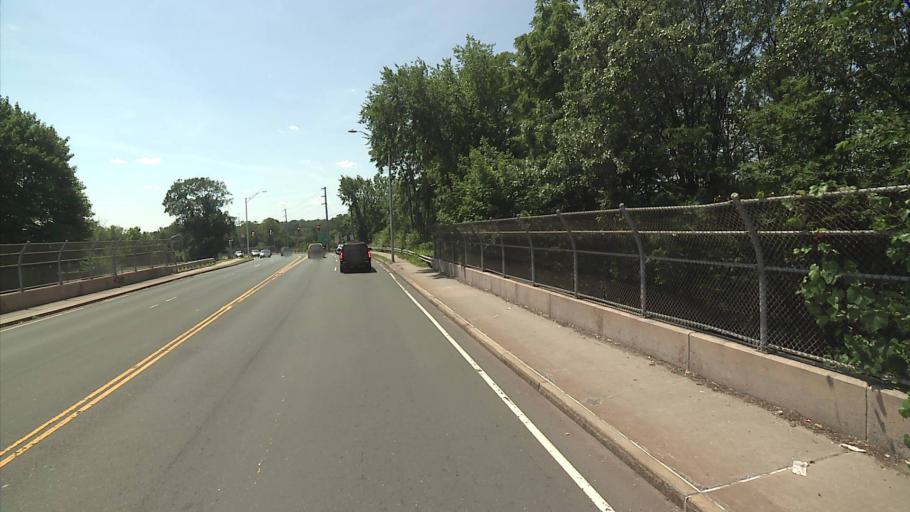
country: US
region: Connecticut
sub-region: Hartford County
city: New Britain
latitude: 41.6655
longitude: -72.8068
